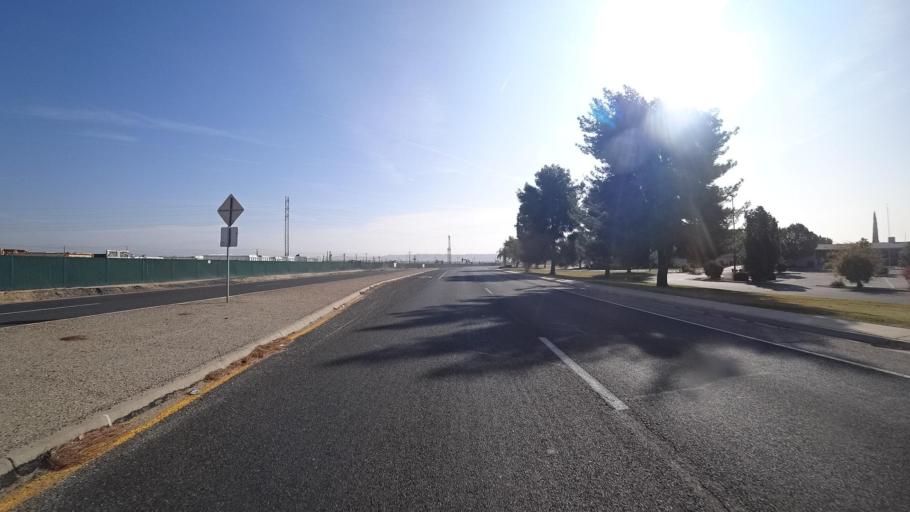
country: US
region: California
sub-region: Kern County
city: Oildale
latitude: 35.4386
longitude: -119.0150
